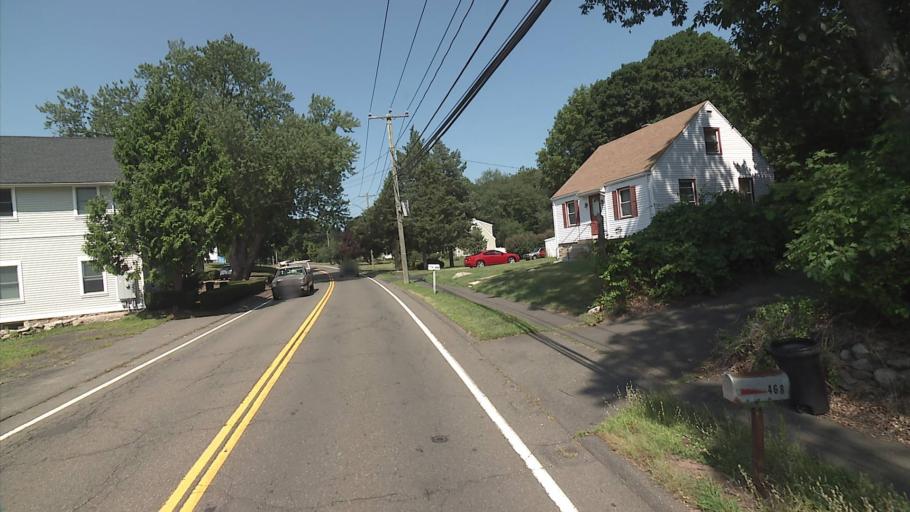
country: US
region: Connecticut
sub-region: New Haven County
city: North Branford
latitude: 41.2742
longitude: -72.7524
